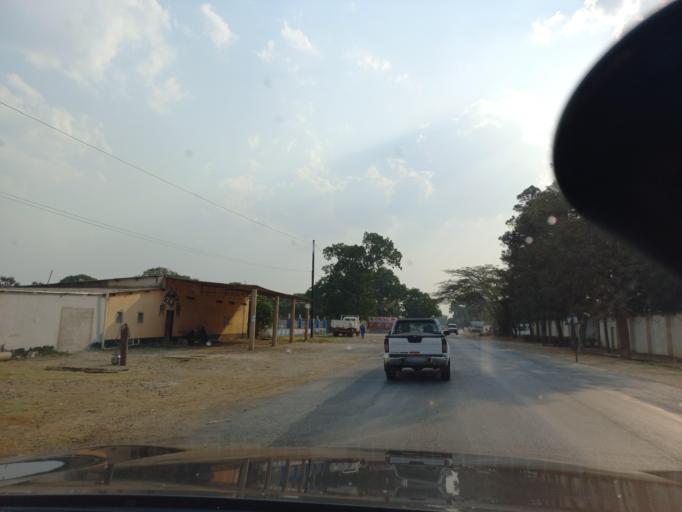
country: ZM
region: Lusaka
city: Lusaka
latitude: -15.4649
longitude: 28.2326
